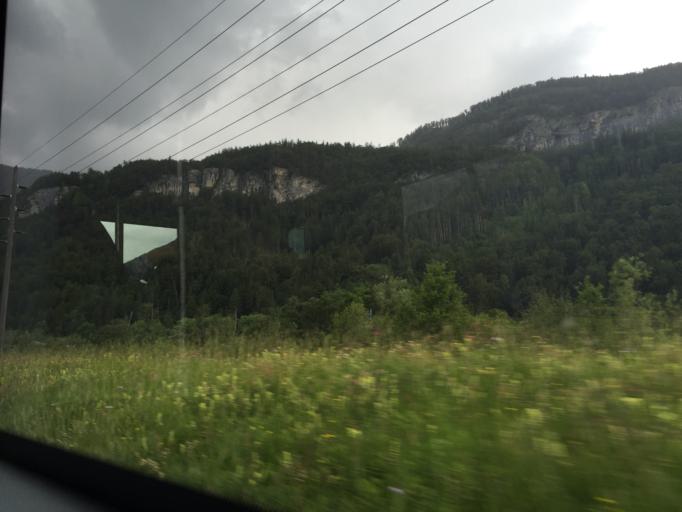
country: CH
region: Bern
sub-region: Interlaken-Oberhasli District
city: Meiringen
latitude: 46.7417
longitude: 8.1455
